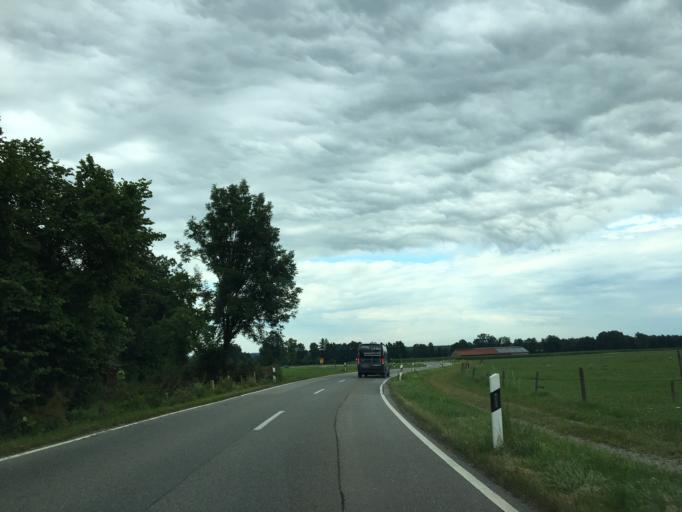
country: DE
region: Bavaria
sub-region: Upper Bavaria
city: Bad Feilnbach
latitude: 47.7788
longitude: 12.0119
